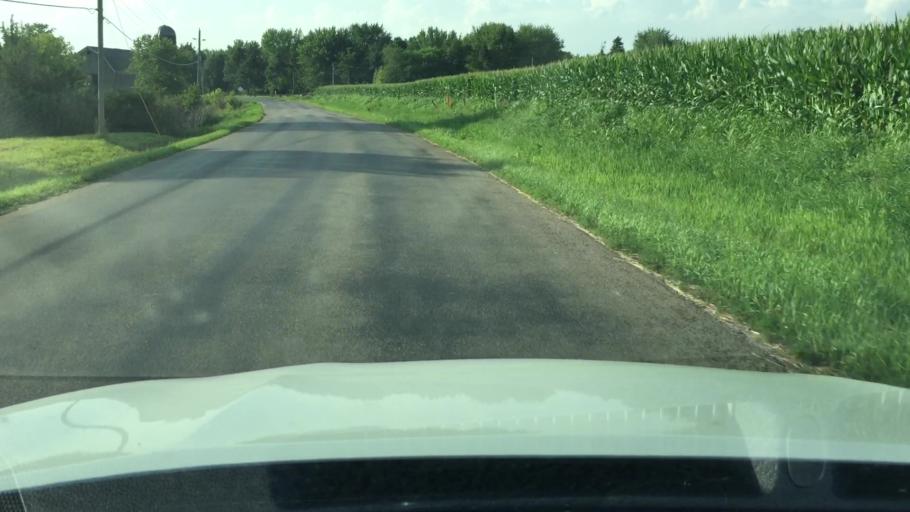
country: US
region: Iowa
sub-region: Johnson County
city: North Liberty
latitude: 41.8131
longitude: -91.6152
